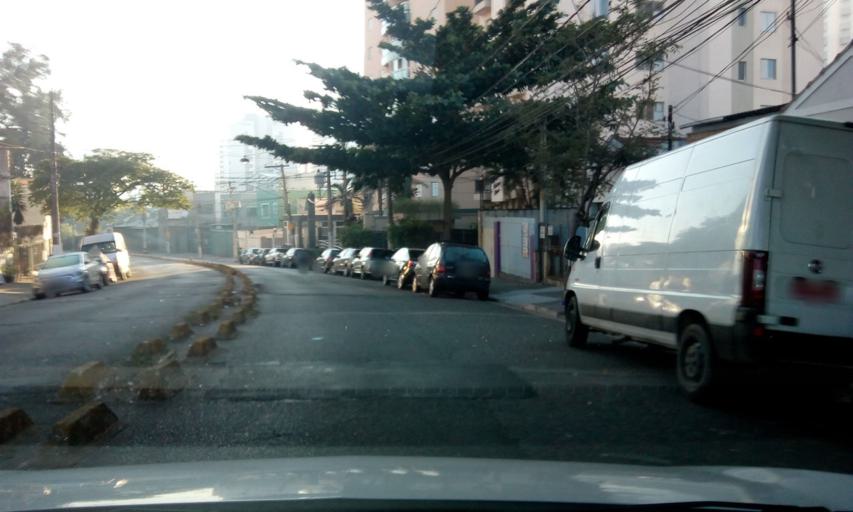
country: BR
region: Sao Paulo
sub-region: Sao Paulo
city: Sao Paulo
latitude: -23.5336
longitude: -46.6942
